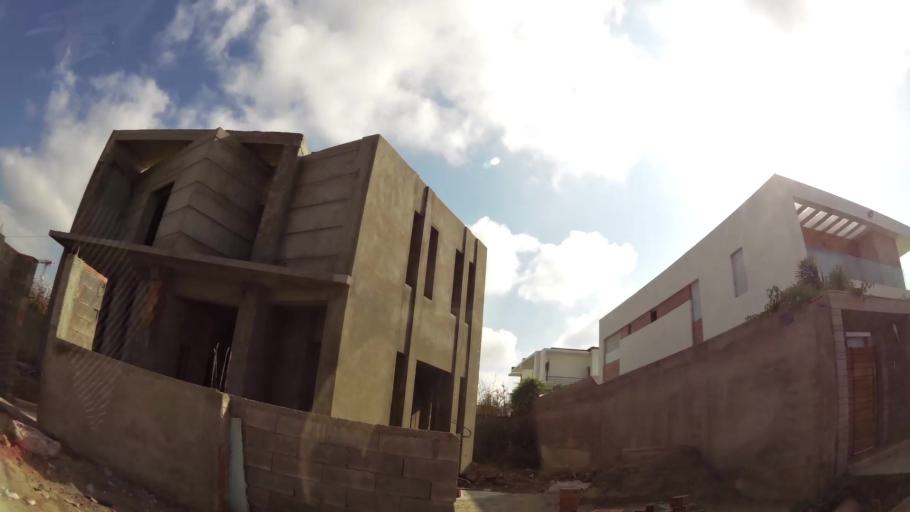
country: MA
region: Rabat-Sale-Zemmour-Zaer
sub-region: Skhirate-Temara
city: Temara
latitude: 33.9529
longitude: -6.8781
